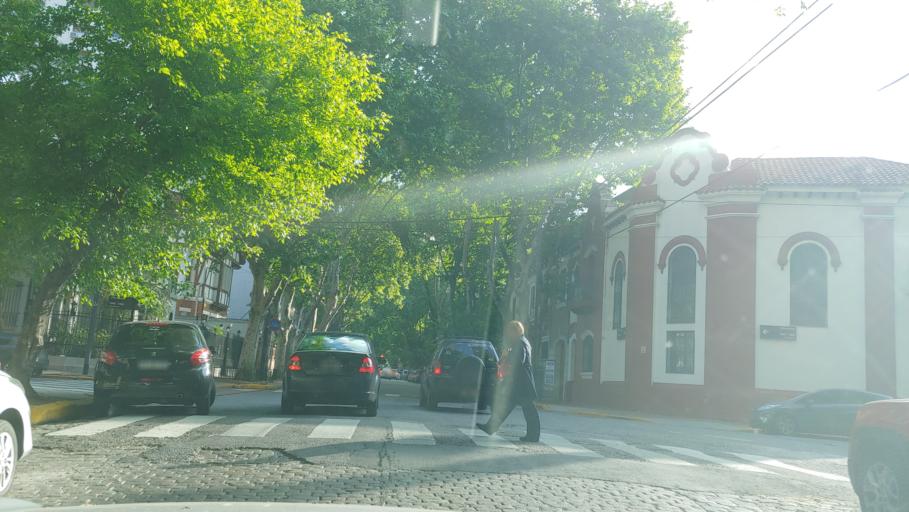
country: AR
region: Buenos Aires F.D.
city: Colegiales
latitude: -34.5657
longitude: -58.4422
